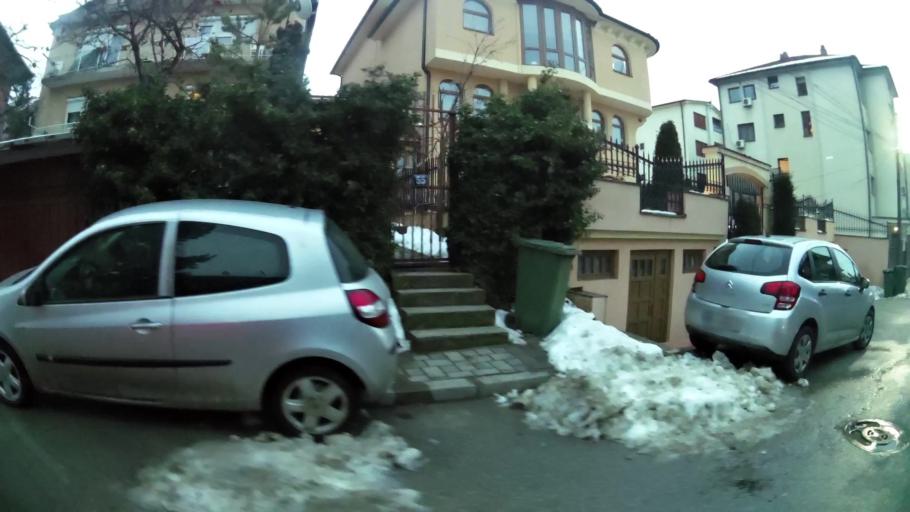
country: XK
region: Pristina
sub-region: Komuna e Prishtines
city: Pristina
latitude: 42.6566
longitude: 21.1718
